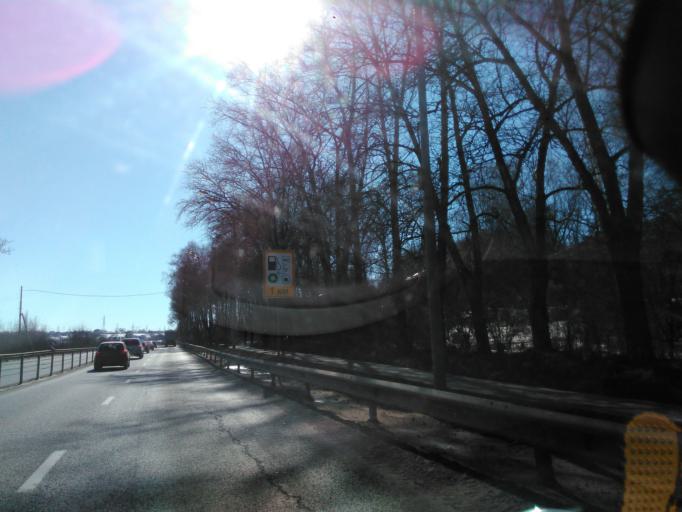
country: RU
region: Moskovskaya
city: Iksha
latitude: 56.1686
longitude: 37.5053
